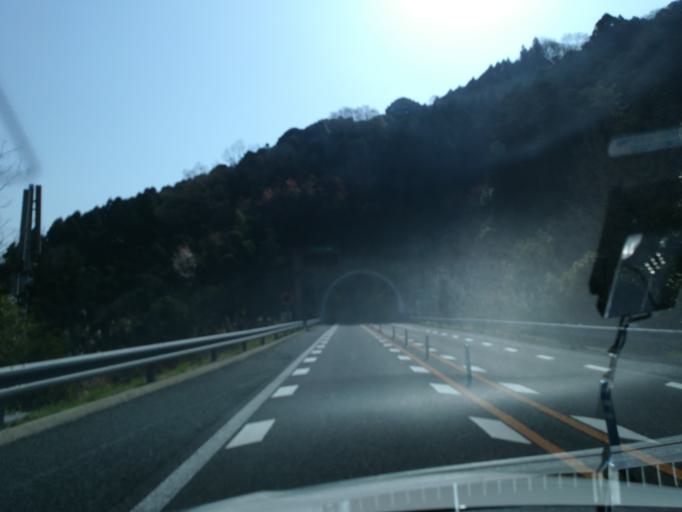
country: JP
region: Tokushima
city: Ikedacho
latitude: 34.0220
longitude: 133.7998
